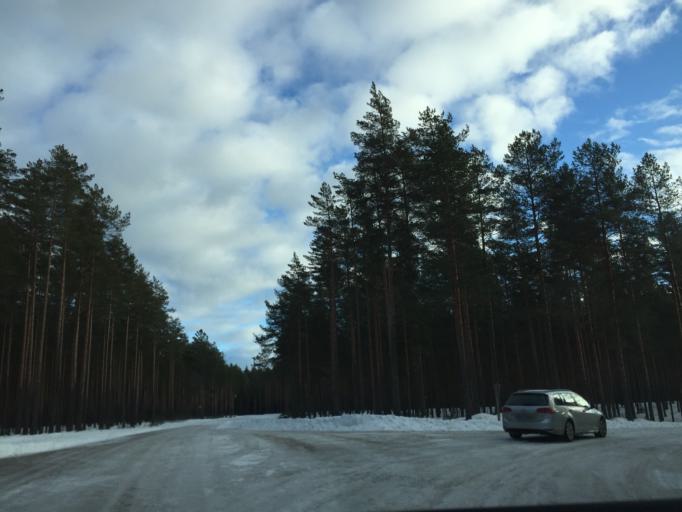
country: LV
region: Ogre
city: Jumprava
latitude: 56.5606
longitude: 24.8544
